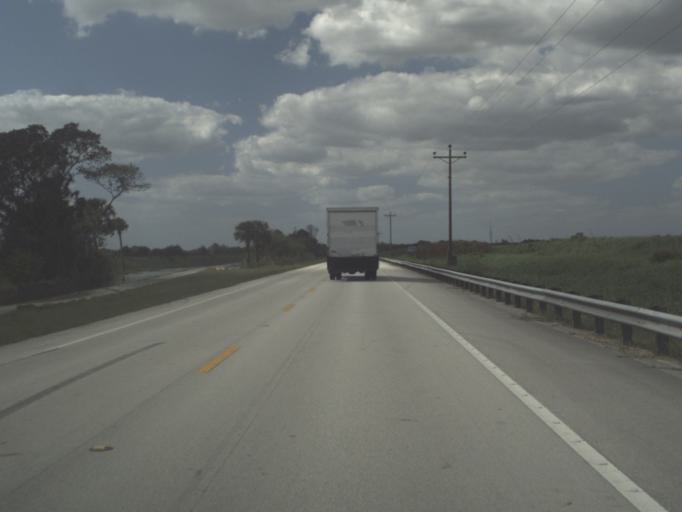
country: US
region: Florida
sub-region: Collier County
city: Lely Resort
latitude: 26.0108
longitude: -81.6172
